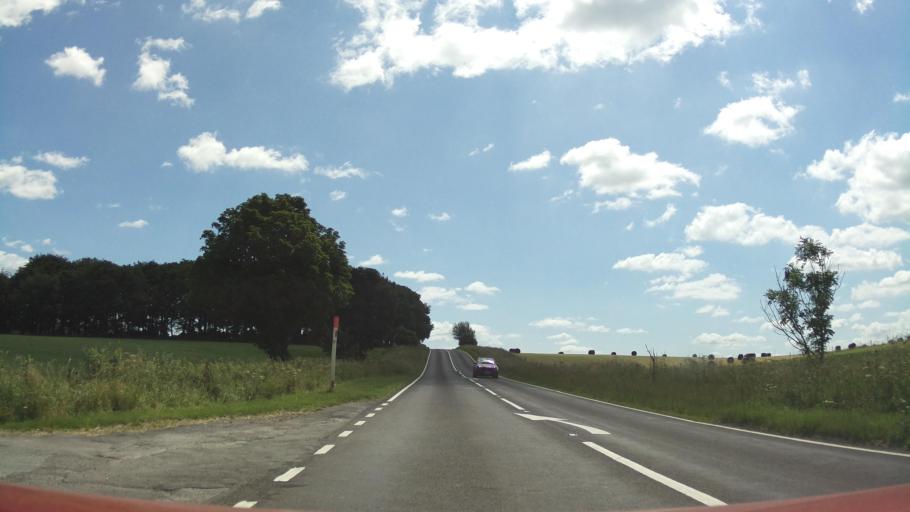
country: GB
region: England
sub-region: Derbyshire
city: Bakewell
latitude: 53.1576
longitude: -1.7721
